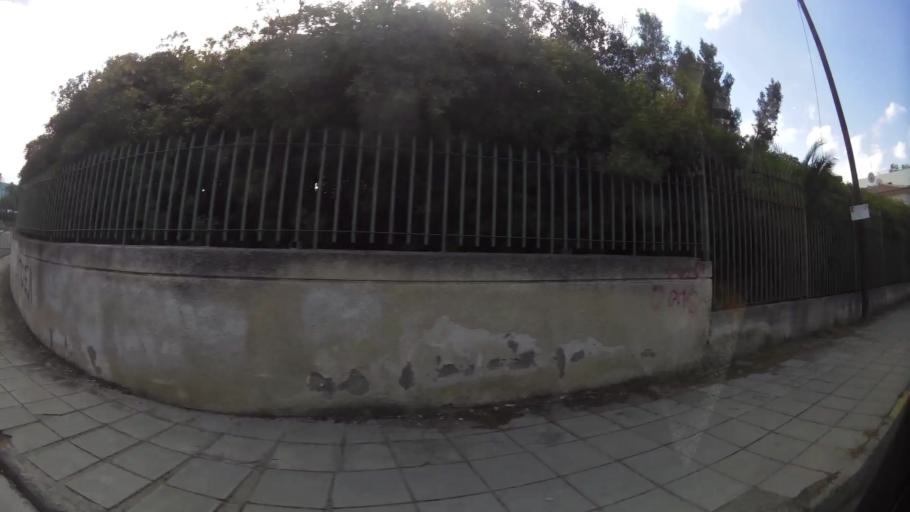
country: CY
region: Lefkosia
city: Nicosia
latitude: 35.1481
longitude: 33.3684
